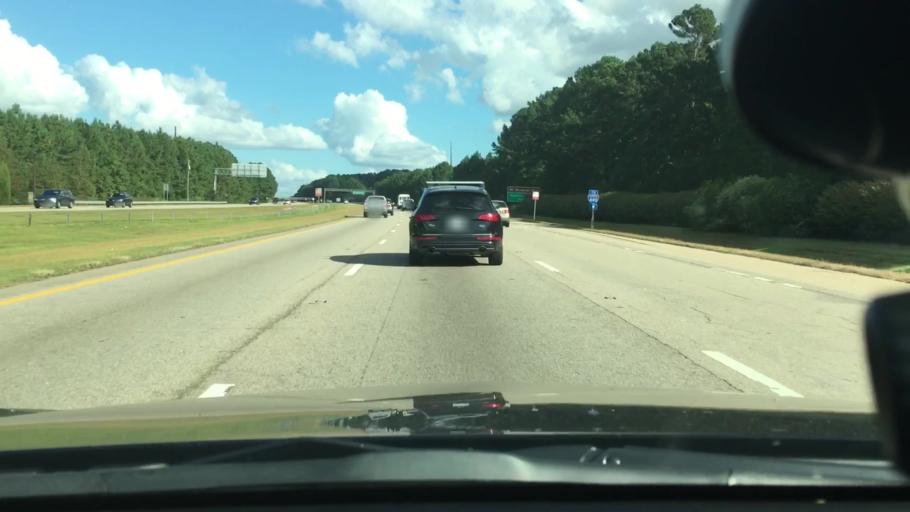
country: US
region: North Carolina
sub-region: Wake County
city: West Raleigh
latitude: 35.8052
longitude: -78.7168
